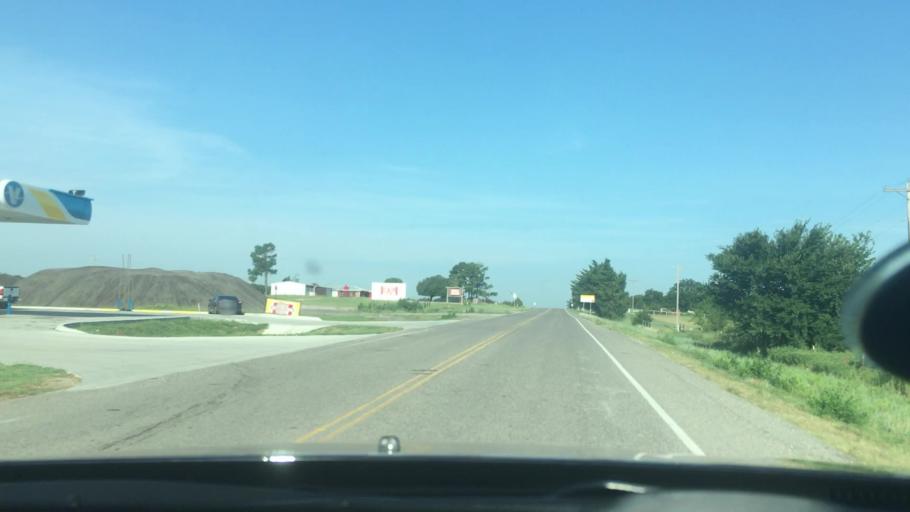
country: US
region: Oklahoma
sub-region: Garvin County
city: Wynnewood
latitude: 34.6517
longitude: -97.2226
